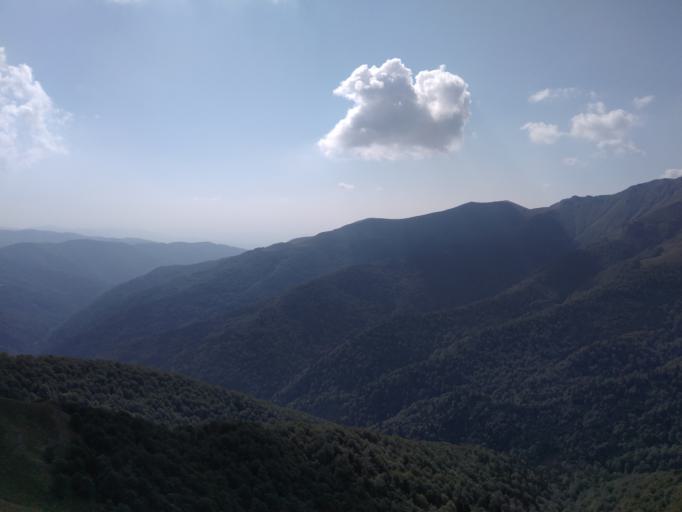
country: BG
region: Stara Zagora
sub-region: Obshtina Pavel Banya
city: Asen
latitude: 42.7517
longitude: 25.0887
